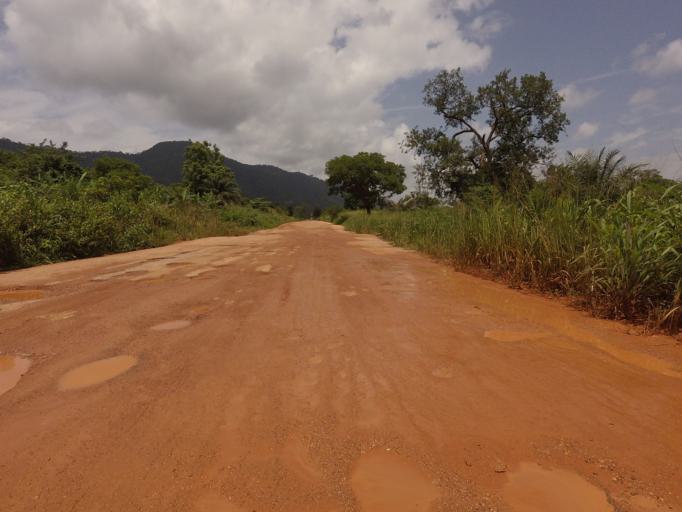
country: GH
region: Volta
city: Ho
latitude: 6.7746
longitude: 0.3644
